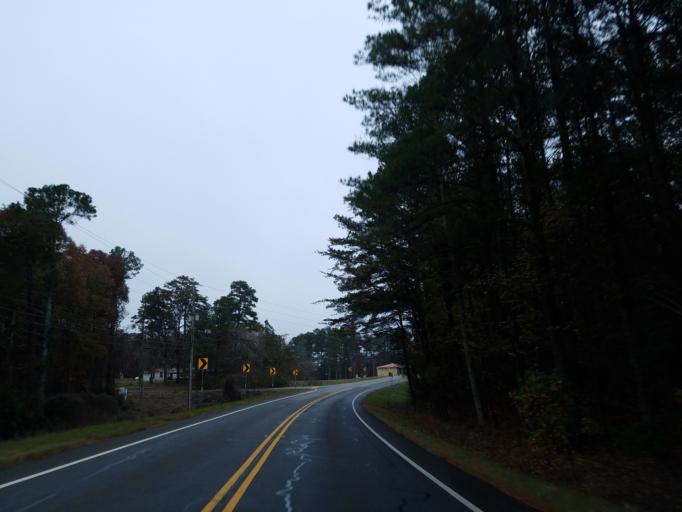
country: US
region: Georgia
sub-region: Pickens County
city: Jasper
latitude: 34.3920
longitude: -84.4667
